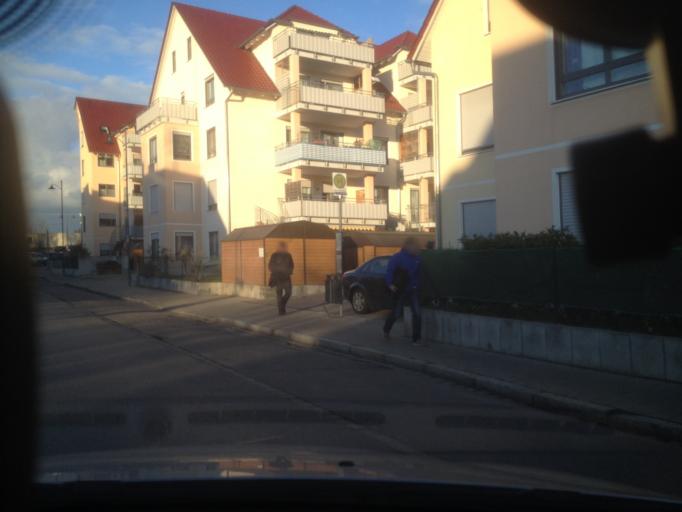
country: DE
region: Bavaria
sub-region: Swabia
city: Mering
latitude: 48.2629
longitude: 10.9848
